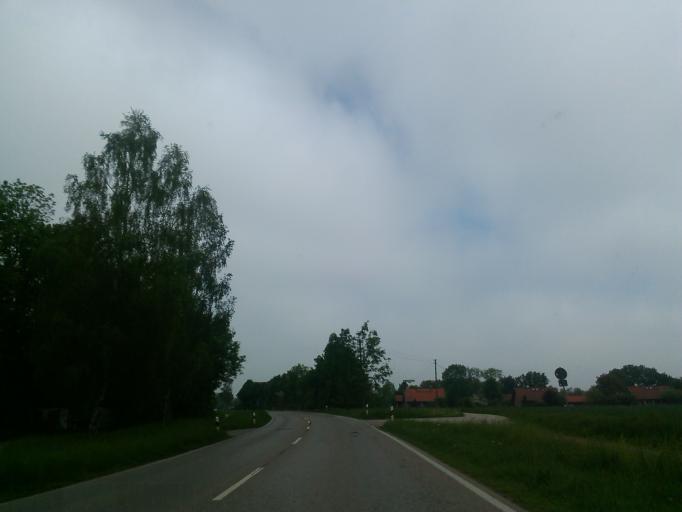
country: DE
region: Bavaria
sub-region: Upper Bavaria
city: Olching
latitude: 48.1861
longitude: 11.3293
